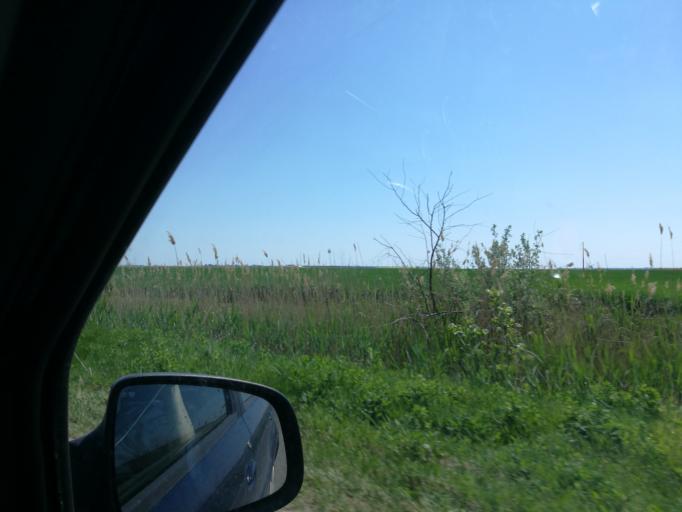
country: RO
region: Ialomita
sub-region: Comuna Adancata
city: Adancata
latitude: 44.7825
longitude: 26.4545
